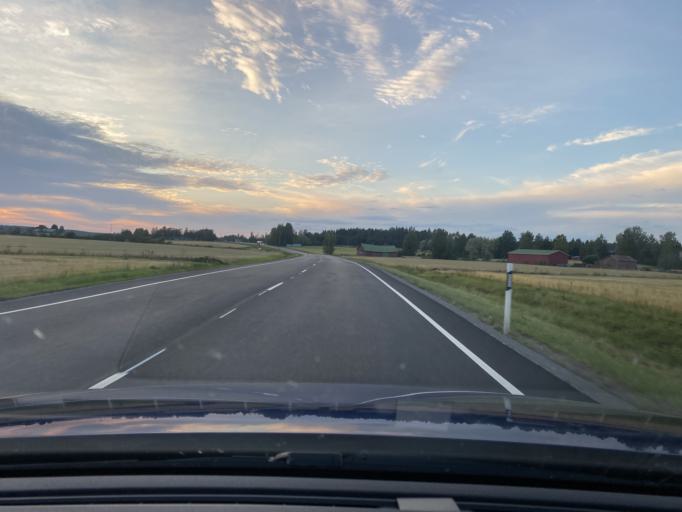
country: FI
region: Satakunta
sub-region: Pohjois-Satakunta
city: Kankaanpaeae
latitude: 61.8376
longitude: 22.3465
